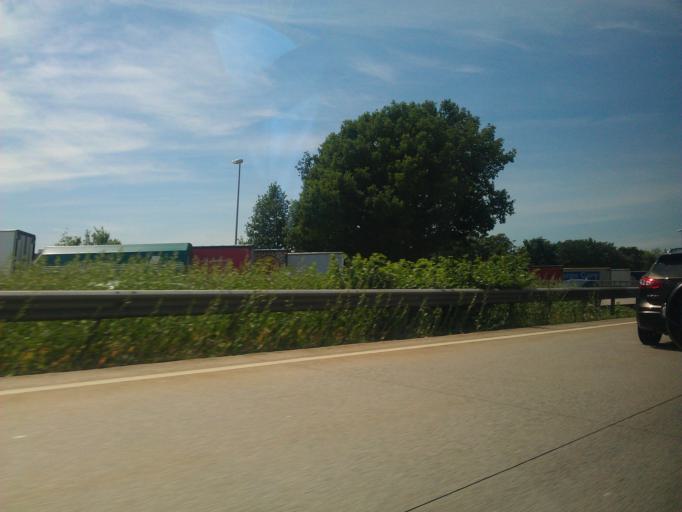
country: DE
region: Rheinland-Pfalz
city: Breitscheid
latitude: 50.5983
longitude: 7.4373
